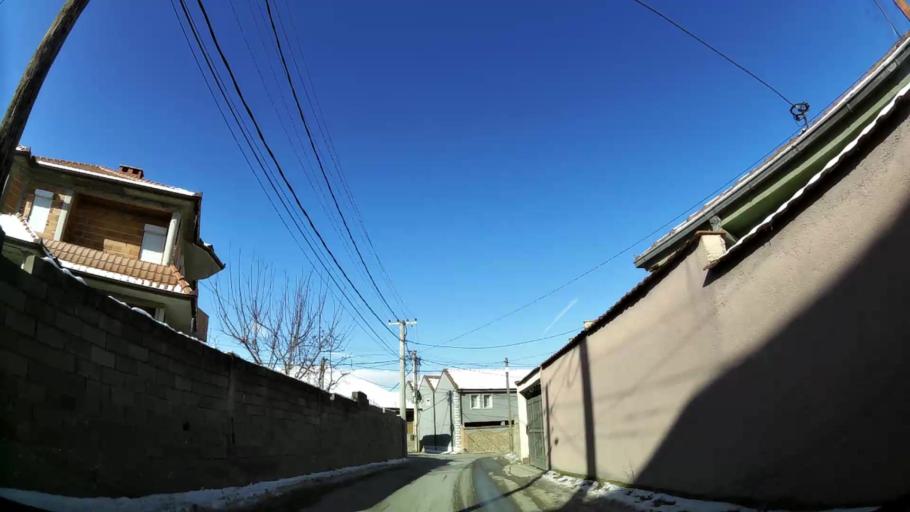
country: MK
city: Grchec
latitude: 41.9928
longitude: 21.3265
